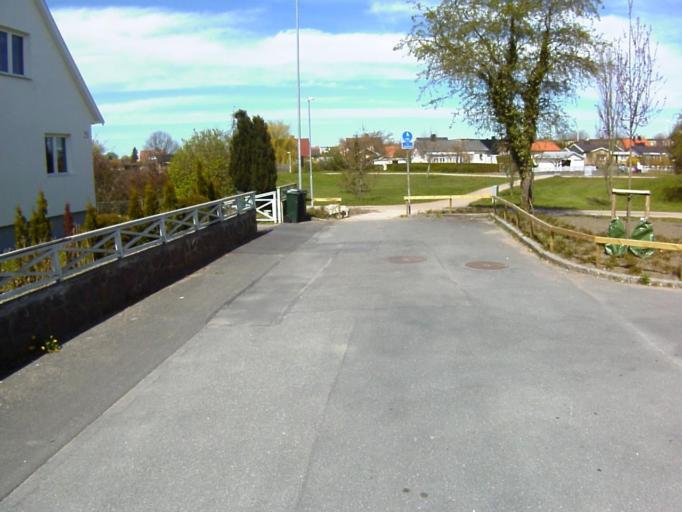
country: SE
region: Skane
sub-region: Kristianstads Kommun
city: Kristianstad
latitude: 56.0537
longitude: 14.1538
